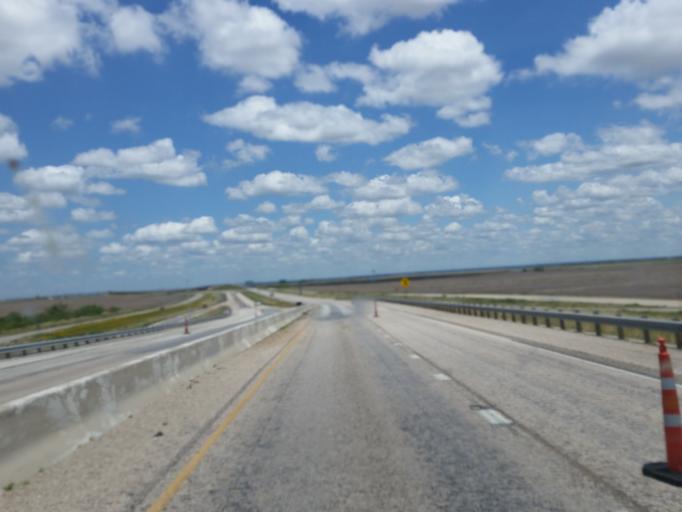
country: US
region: Texas
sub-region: Nolan County
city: Roscoe
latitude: 32.4490
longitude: -100.5184
